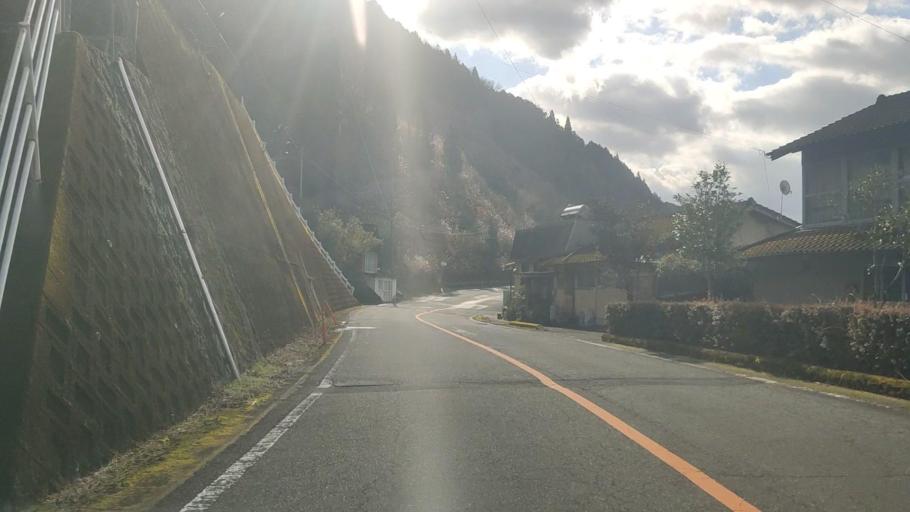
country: JP
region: Kumamoto
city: Hitoyoshi
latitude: 32.3131
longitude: 130.8474
